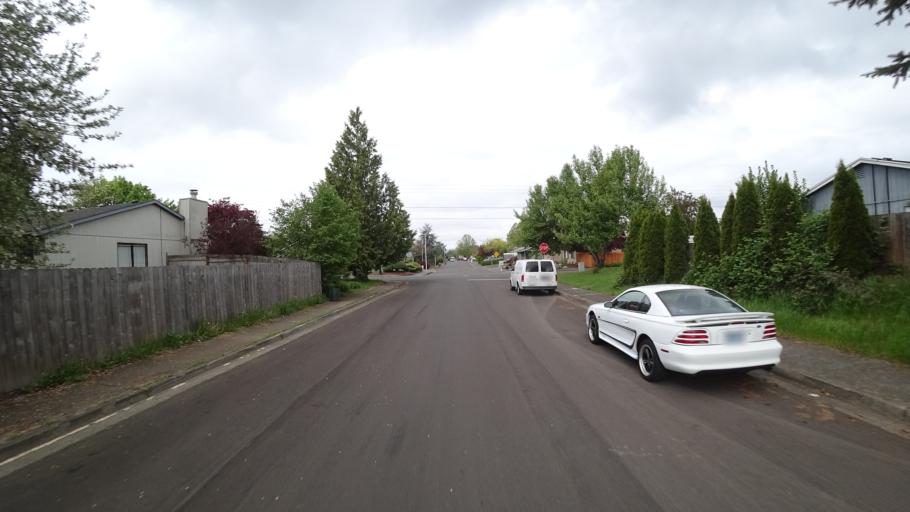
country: US
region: Oregon
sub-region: Washington County
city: Hillsboro
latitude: 45.5402
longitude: -122.9750
